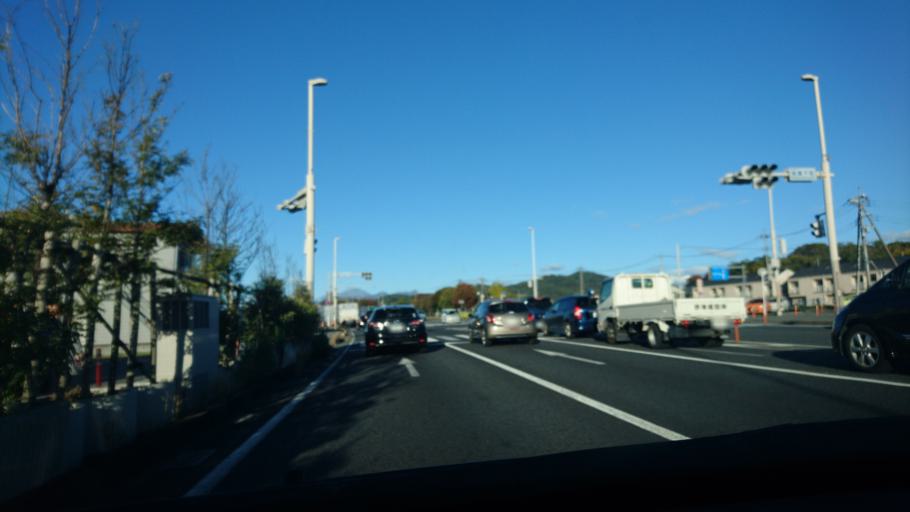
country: JP
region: Gunma
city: Annaka
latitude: 36.3358
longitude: 138.9416
